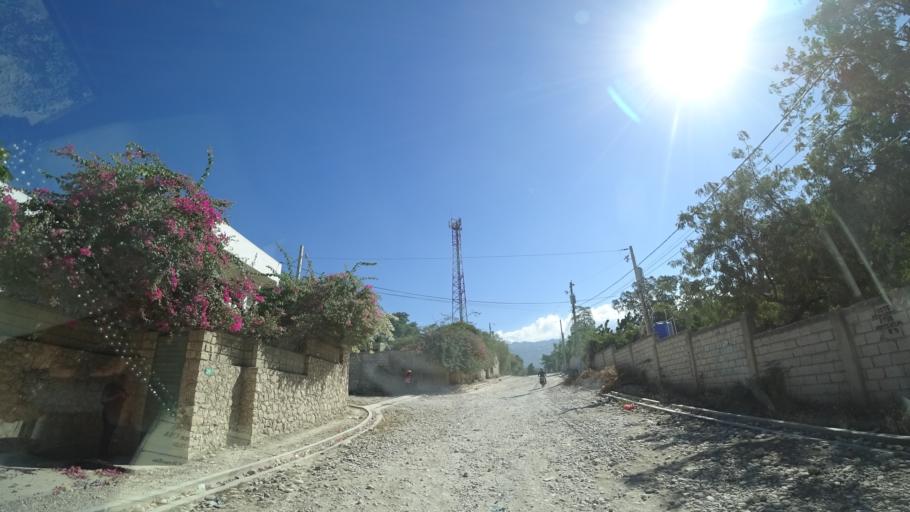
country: HT
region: Ouest
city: Delmas 73
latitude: 18.5481
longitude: -72.2871
